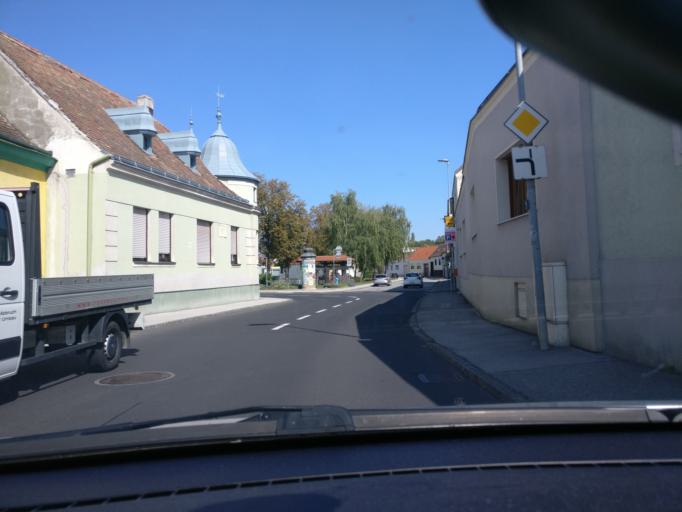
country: AT
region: Burgenland
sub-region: Politischer Bezirk Mattersburg
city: Mattersburg
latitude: 47.7342
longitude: 16.3934
